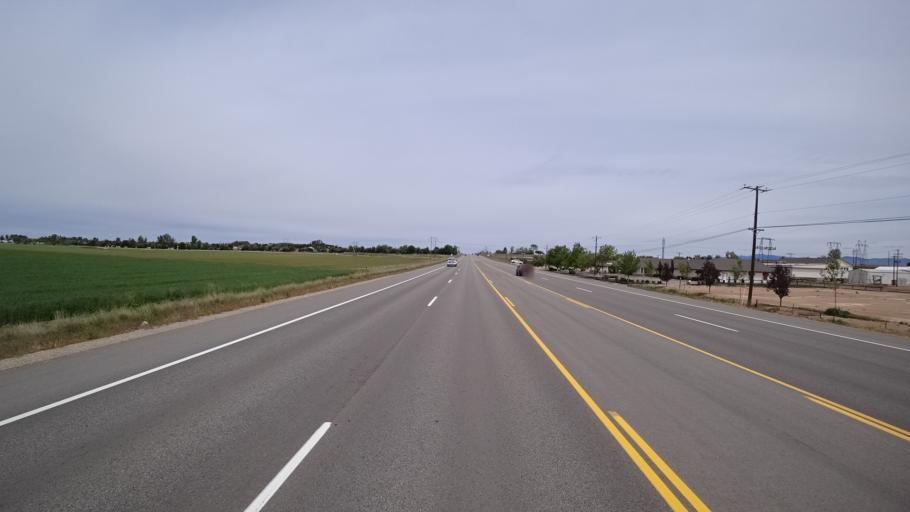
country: US
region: Idaho
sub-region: Ada County
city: Kuna
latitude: 43.5348
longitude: -116.3940
